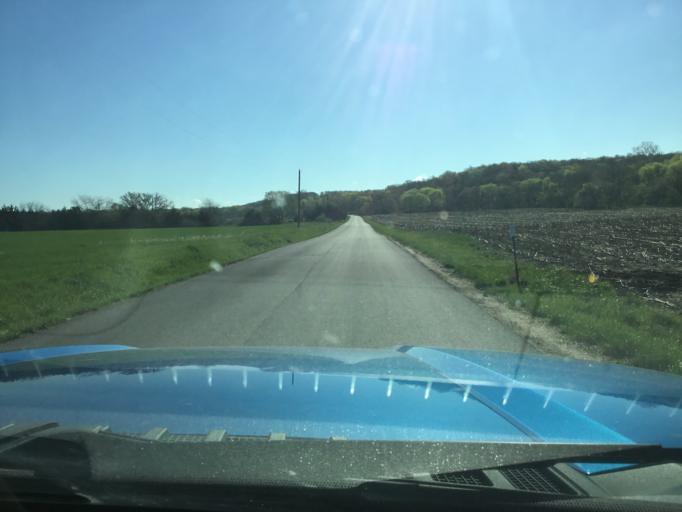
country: US
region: Kansas
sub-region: Douglas County
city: Lawrence
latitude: 38.9933
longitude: -95.3163
